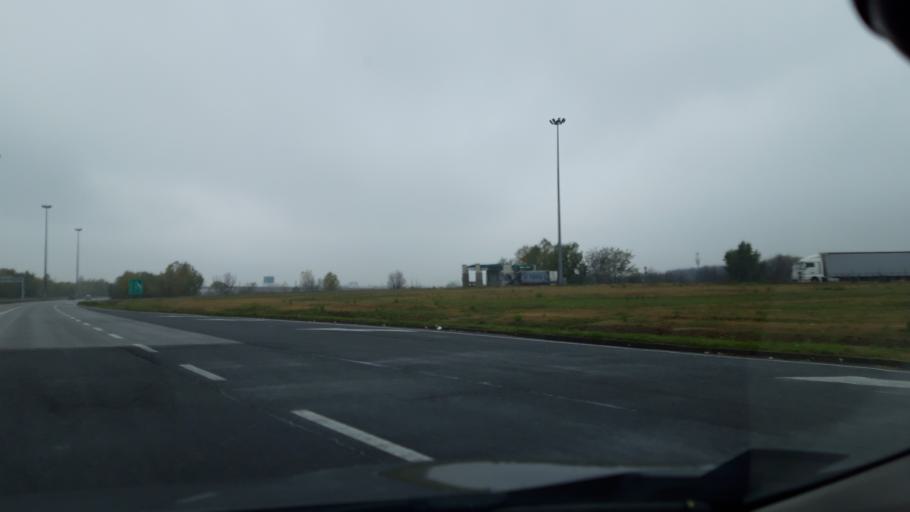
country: HU
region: Csongrad
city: Roszke
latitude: 46.1720
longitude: 19.9744
